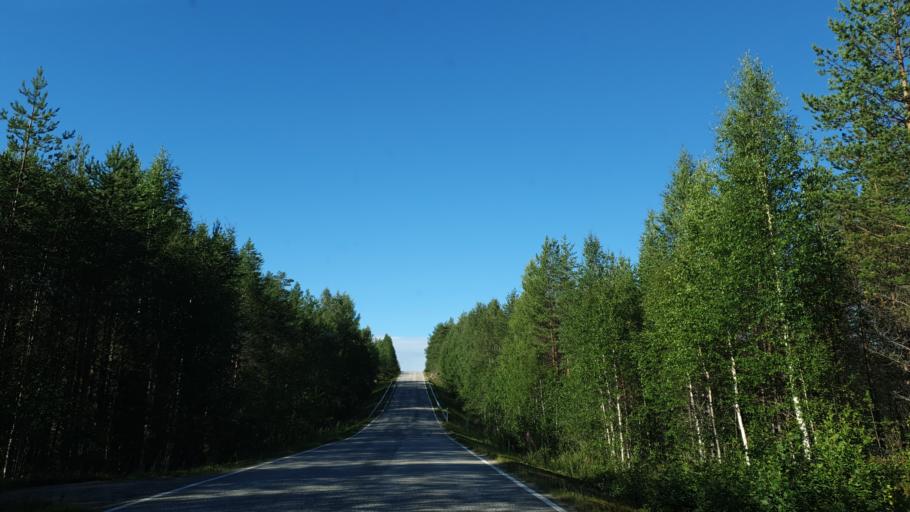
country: FI
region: Kainuu
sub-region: Kehys-Kainuu
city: Kuhmo
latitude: 64.3059
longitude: 29.4220
